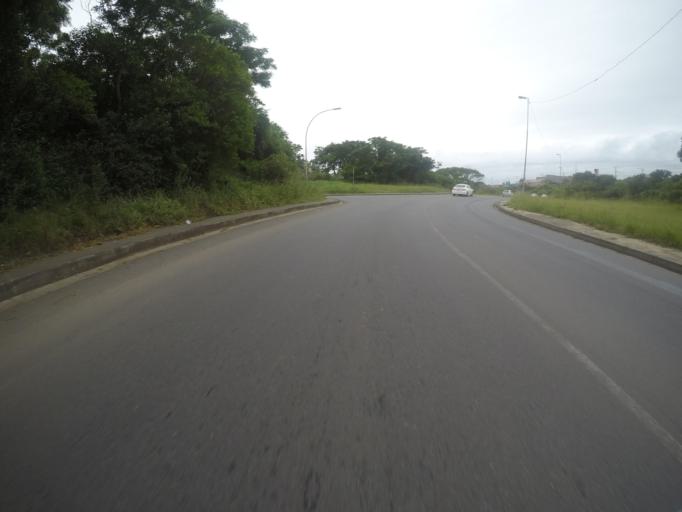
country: ZA
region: Eastern Cape
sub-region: Buffalo City Metropolitan Municipality
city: East London
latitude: -32.9738
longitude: 27.8907
